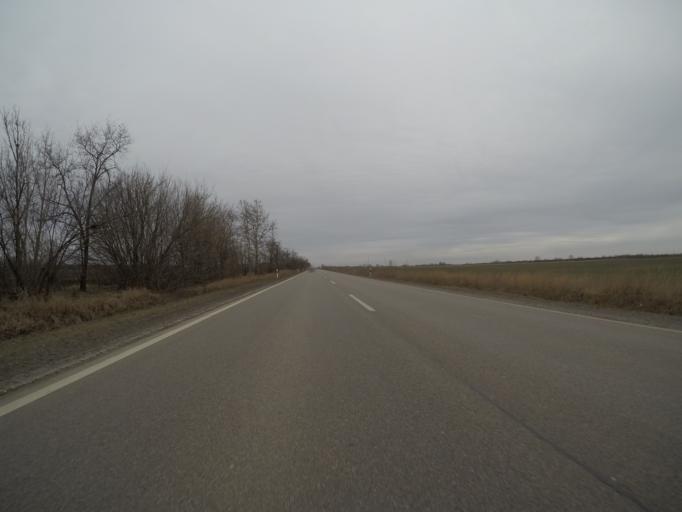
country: HU
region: Jasz-Nagykun-Szolnok
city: Jaszapati
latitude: 47.5317
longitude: 20.1697
